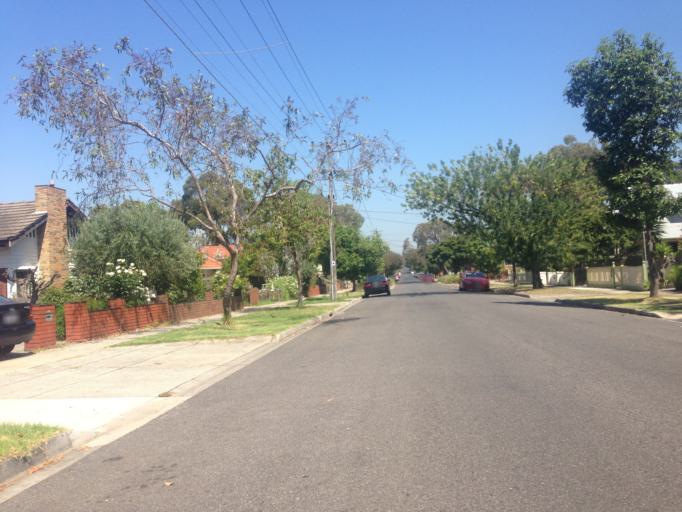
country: AU
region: Victoria
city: Thornbury
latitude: -37.7532
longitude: 144.9910
